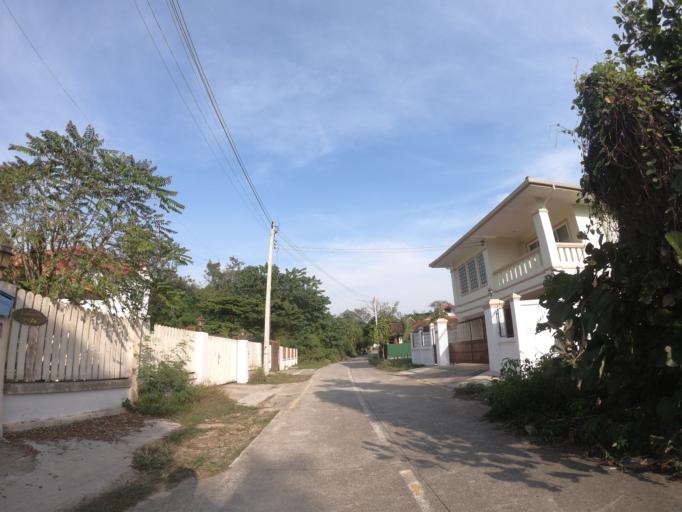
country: TH
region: Chiang Mai
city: Saraphi
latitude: 18.7334
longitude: 98.9835
